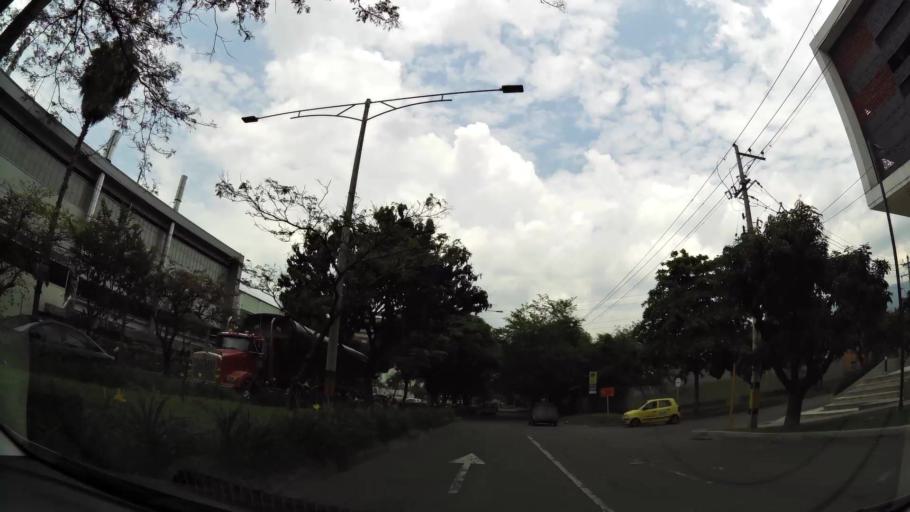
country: CO
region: Antioquia
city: Envigado
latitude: 6.1636
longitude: -75.6019
